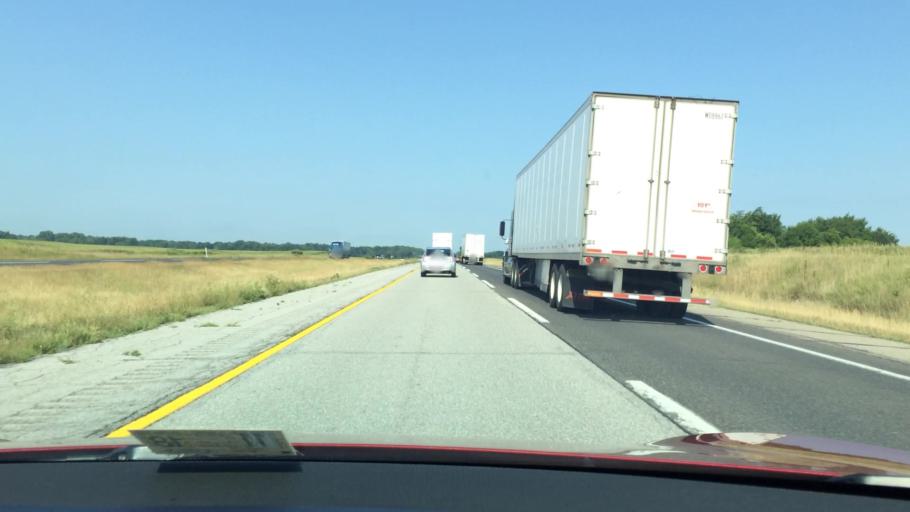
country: US
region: Michigan
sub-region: Branch County
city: Bronson
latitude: 41.7562
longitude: -85.1904
